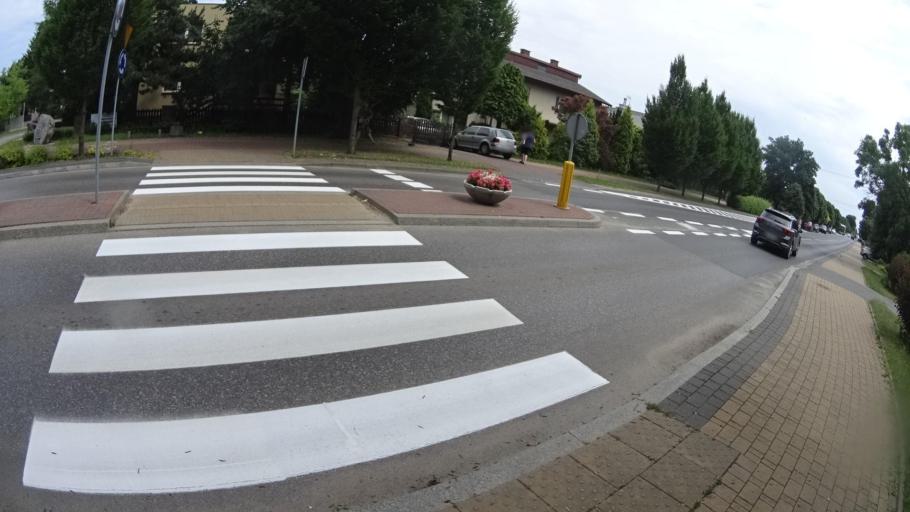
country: PL
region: Masovian Voivodeship
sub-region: Powiat grojecki
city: Grojec
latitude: 51.8599
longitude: 20.8685
